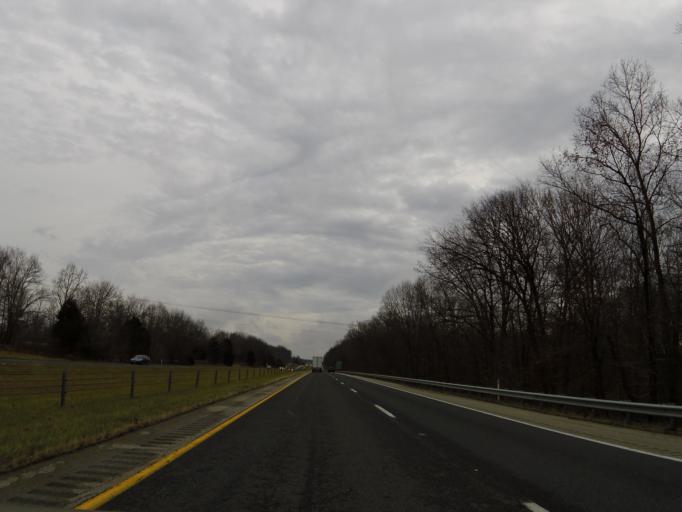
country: US
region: Indiana
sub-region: Ripley County
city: Sunman
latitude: 39.2804
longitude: -85.1198
